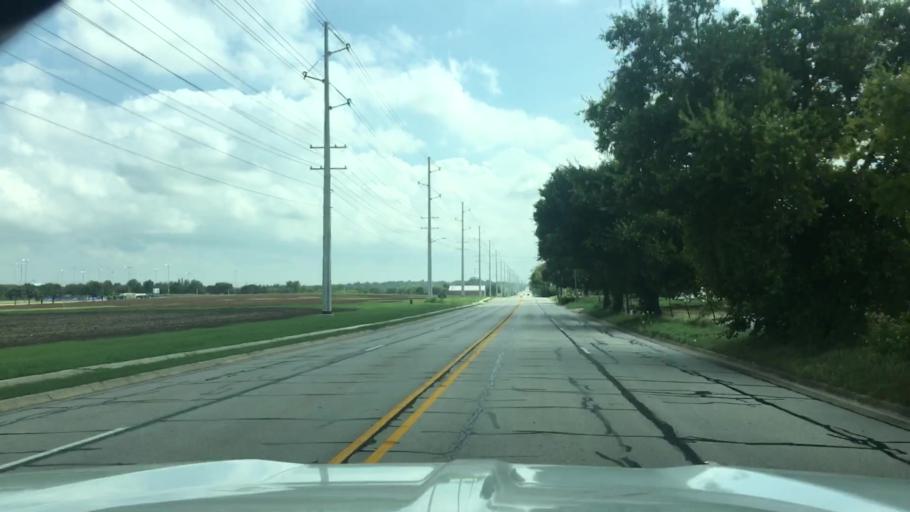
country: US
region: Texas
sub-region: Denton County
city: Denton
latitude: 33.2462
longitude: -97.1606
